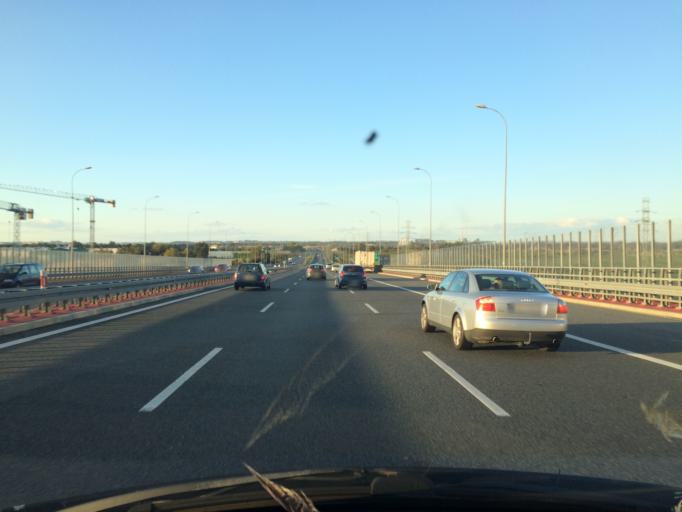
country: PL
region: Lesser Poland Voivodeship
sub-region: Powiat wielicki
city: Czarnochowice
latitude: 50.0184
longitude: 20.0618
